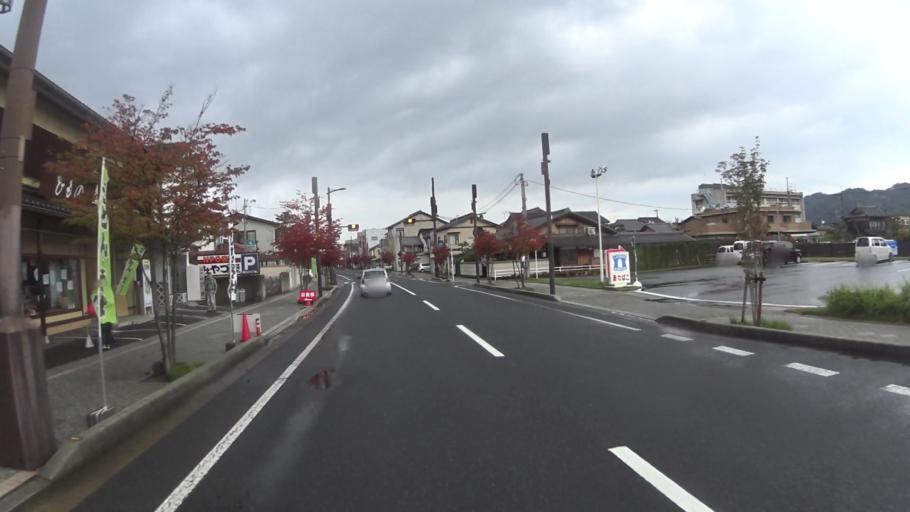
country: JP
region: Kyoto
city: Miyazu
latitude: 35.5328
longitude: 135.1929
